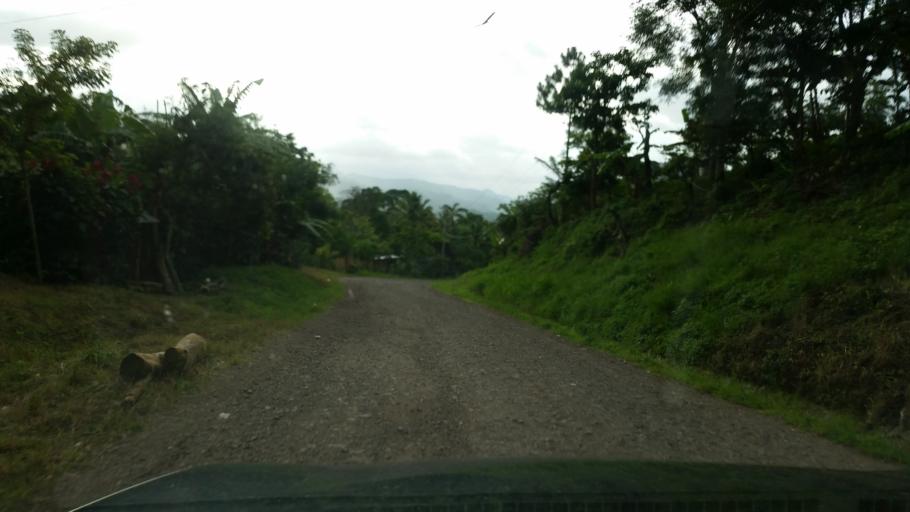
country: NI
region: Jinotega
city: Jinotega
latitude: 13.2435
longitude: -85.7289
